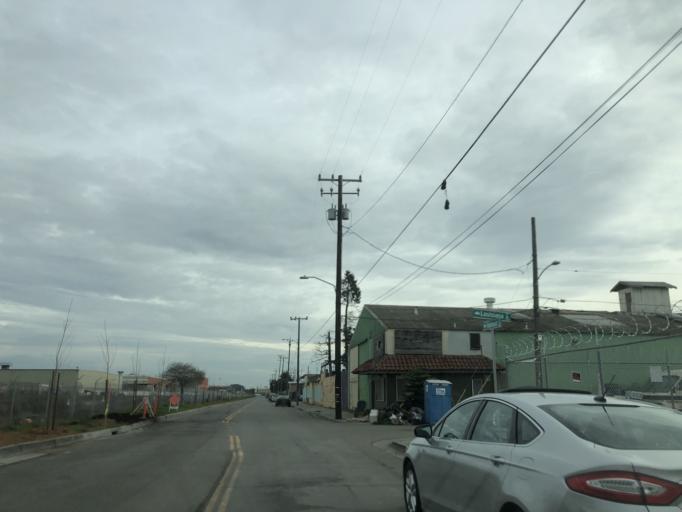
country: US
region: California
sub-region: Alameda County
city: San Leandro
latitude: 37.7408
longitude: -122.1856
